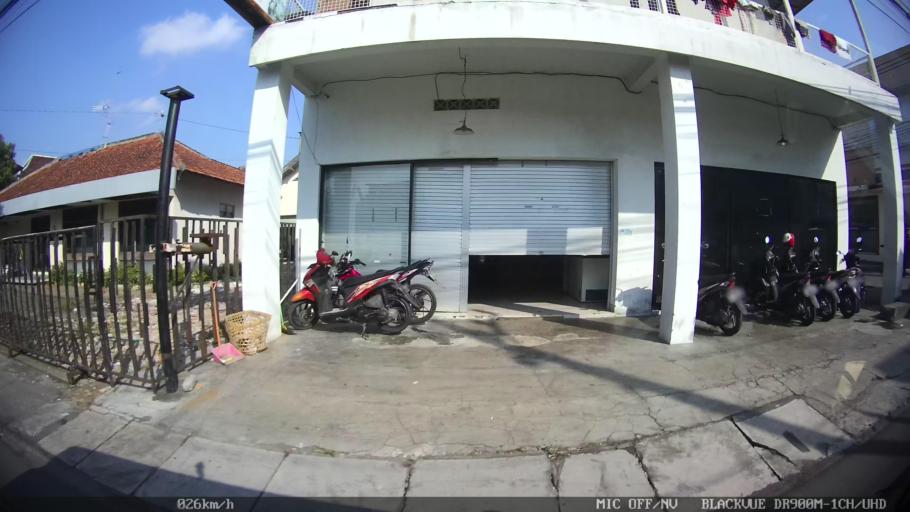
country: ID
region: Daerah Istimewa Yogyakarta
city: Depok
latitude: -7.7724
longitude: 110.4015
